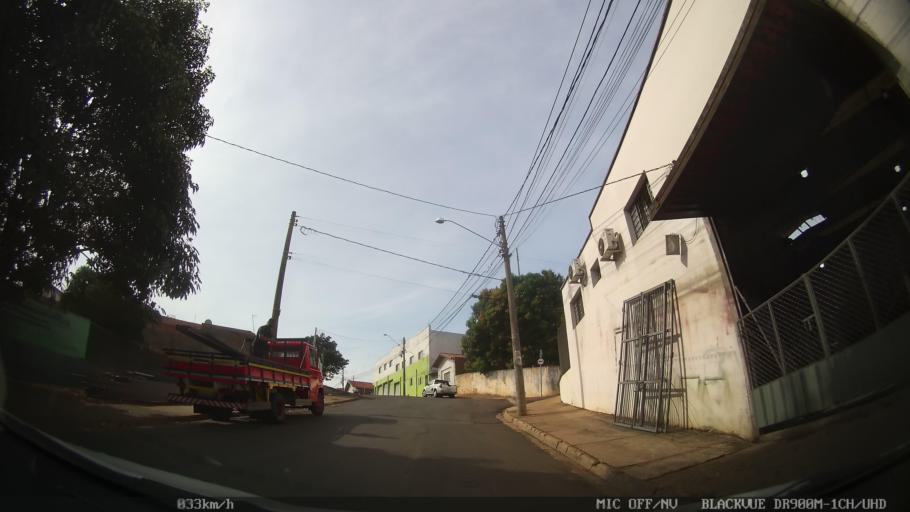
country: BR
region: Sao Paulo
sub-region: Piracicaba
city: Piracicaba
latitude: -22.7448
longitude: -47.6555
